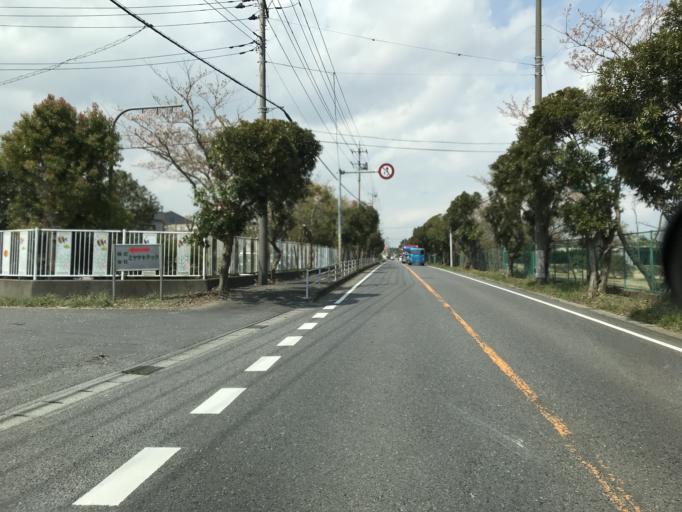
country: JP
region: Chiba
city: Omigawa
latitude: 35.8578
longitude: 140.5566
